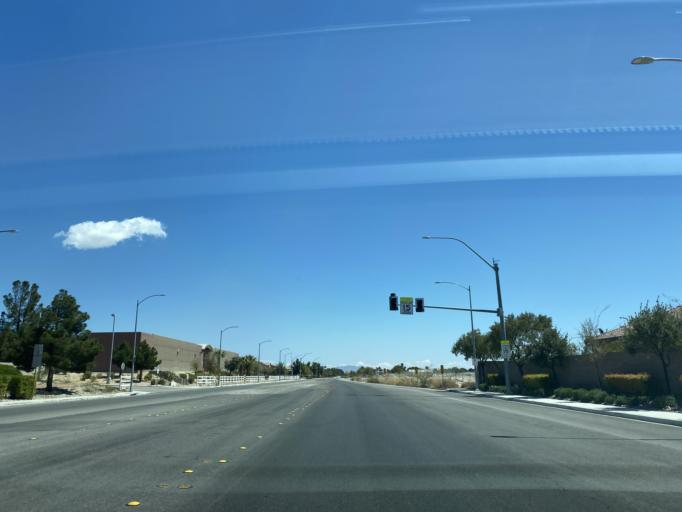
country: US
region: Nevada
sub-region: Clark County
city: North Las Vegas
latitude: 36.3050
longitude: -115.2361
